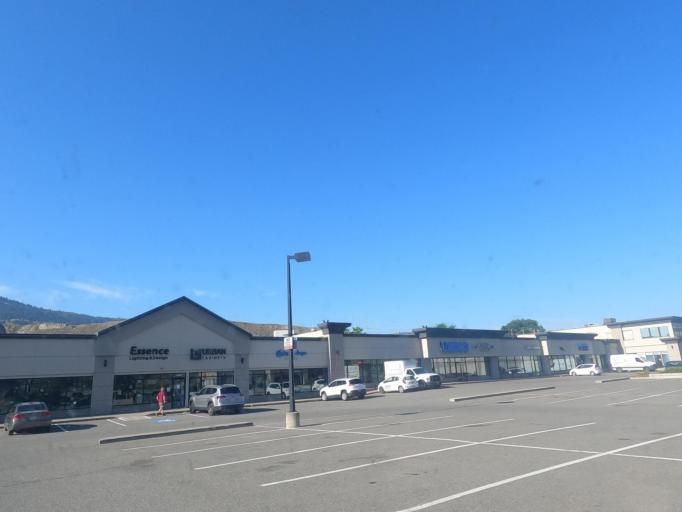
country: CA
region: British Columbia
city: Kamloops
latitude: 50.6797
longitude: -120.2729
